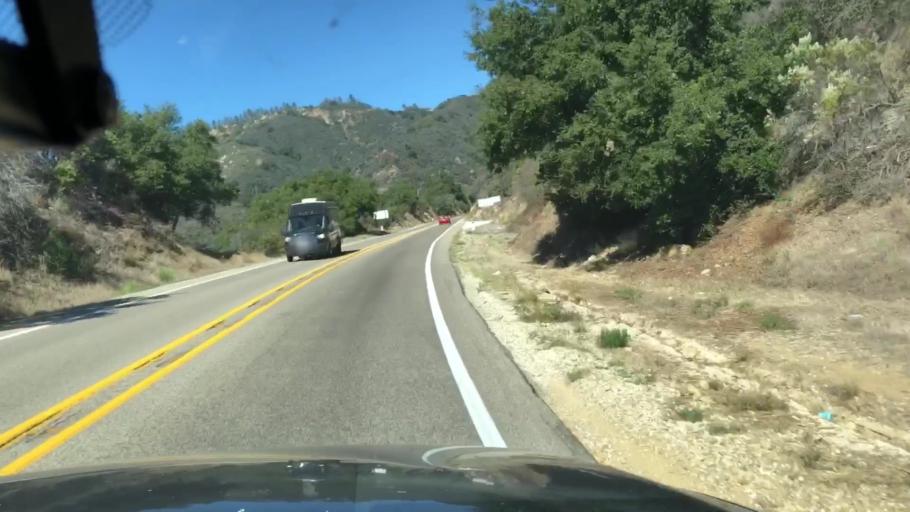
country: US
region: California
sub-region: Santa Barbara County
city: Goleta
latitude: 34.4960
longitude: -119.8007
